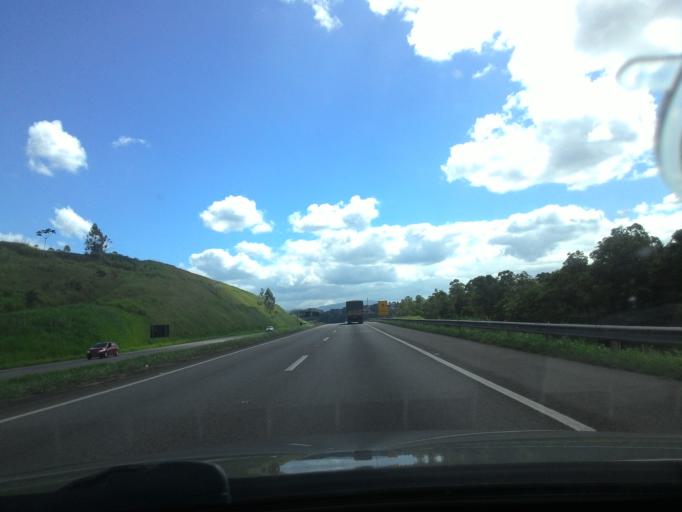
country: BR
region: Sao Paulo
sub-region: Cajati
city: Cajati
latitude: -24.7264
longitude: -48.0905
